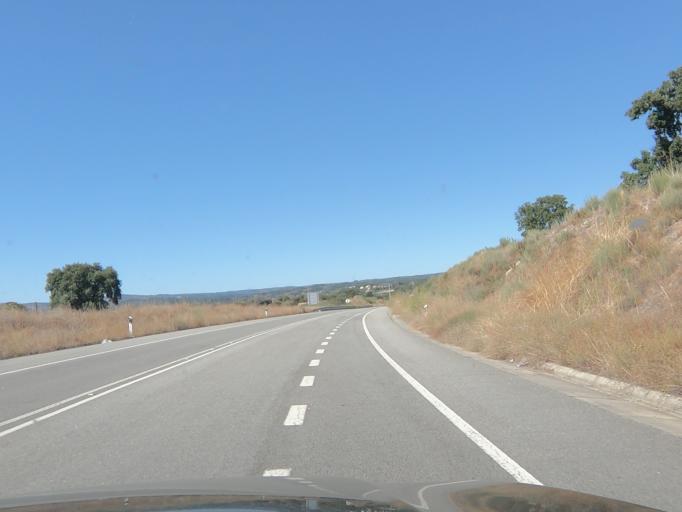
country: PT
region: Vila Real
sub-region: Valpacos
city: Valpacos
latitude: 41.5736
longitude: -7.3004
